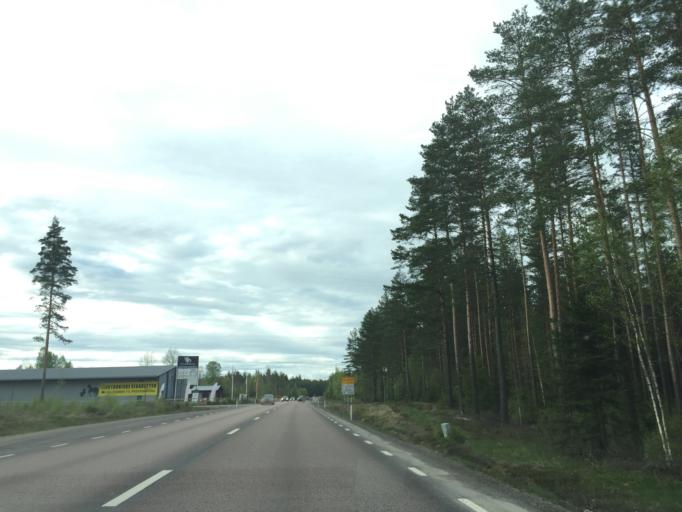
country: SE
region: Vaermland
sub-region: Eda Kommun
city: Charlottenberg
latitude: 59.8903
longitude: 12.2809
